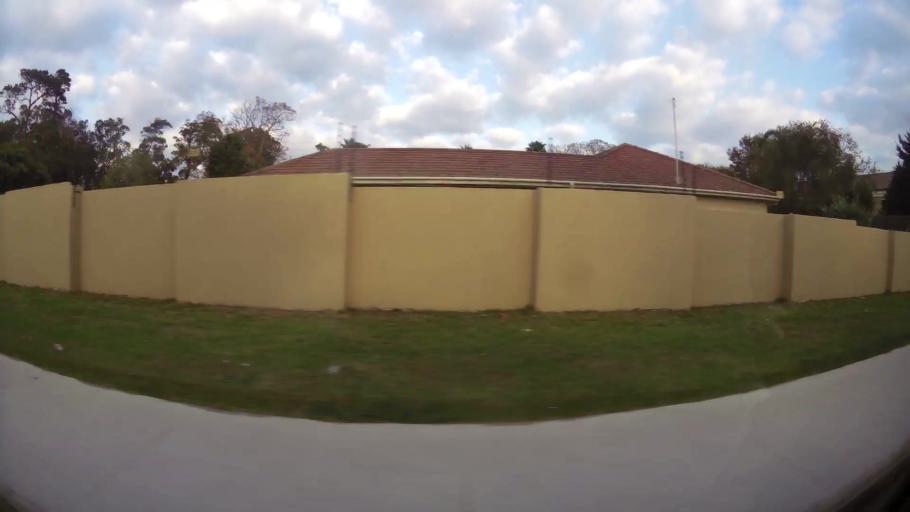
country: ZA
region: Eastern Cape
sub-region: Nelson Mandela Bay Metropolitan Municipality
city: Port Elizabeth
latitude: -33.9829
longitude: 25.5813
